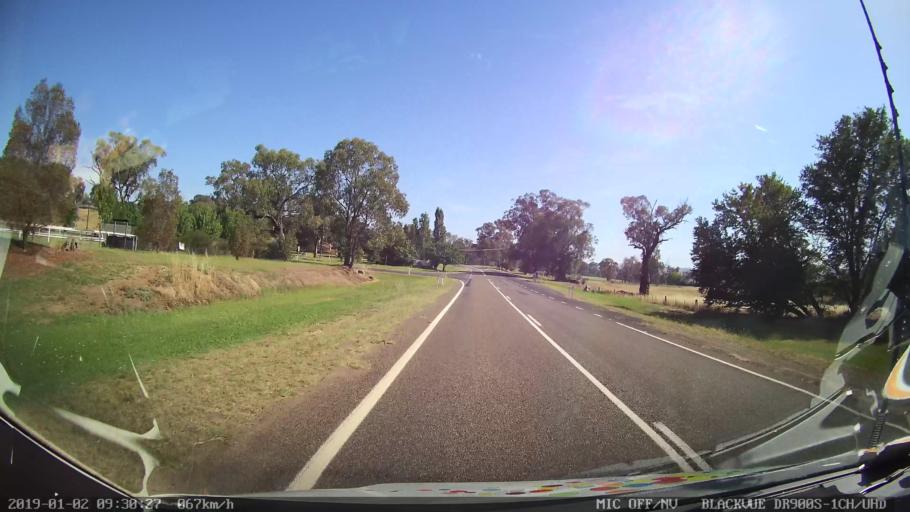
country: AU
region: New South Wales
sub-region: Tumut Shire
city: Tumut
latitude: -35.3265
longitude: 148.2378
